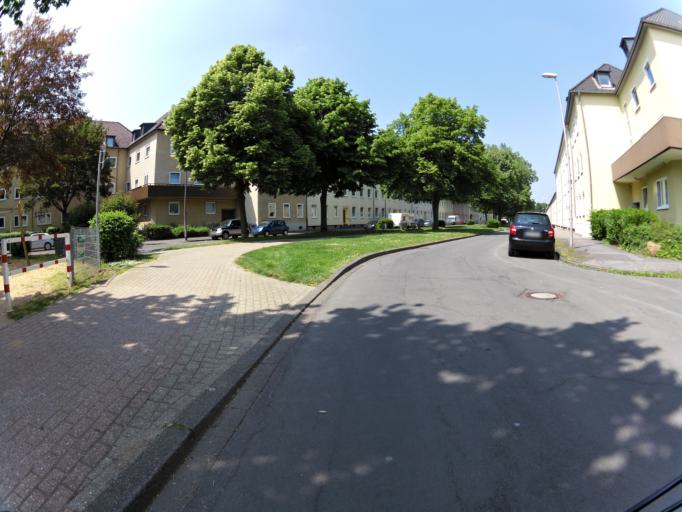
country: DE
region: North Rhine-Westphalia
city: Julich
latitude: 50.9155
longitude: 6.3632
